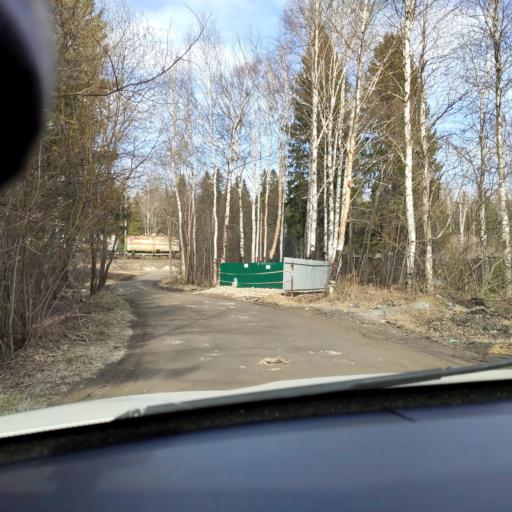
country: RU
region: Perm
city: Overyata
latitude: 58.0598
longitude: 55.9873
